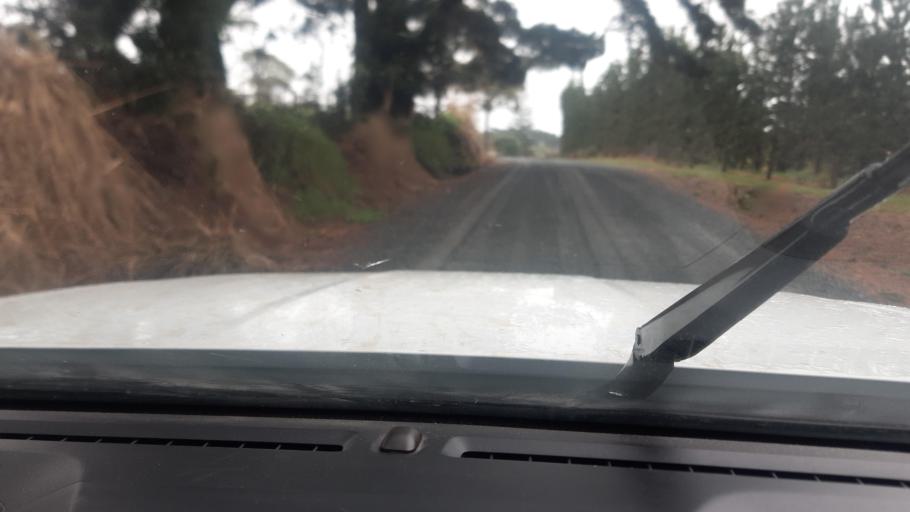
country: NZ
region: Northland
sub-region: Far North District
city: Kaitaia
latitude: -34.9756
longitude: 173.2044
